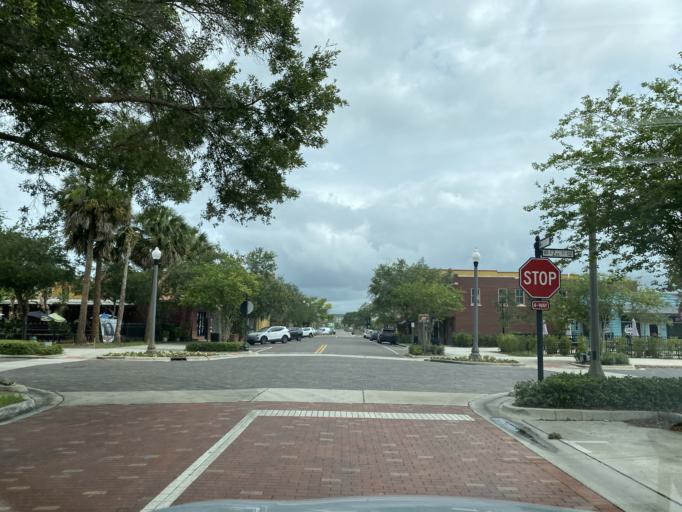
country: US
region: Florida
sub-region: Seminole County
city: Sanford
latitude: 28.8106
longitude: -81.2660
